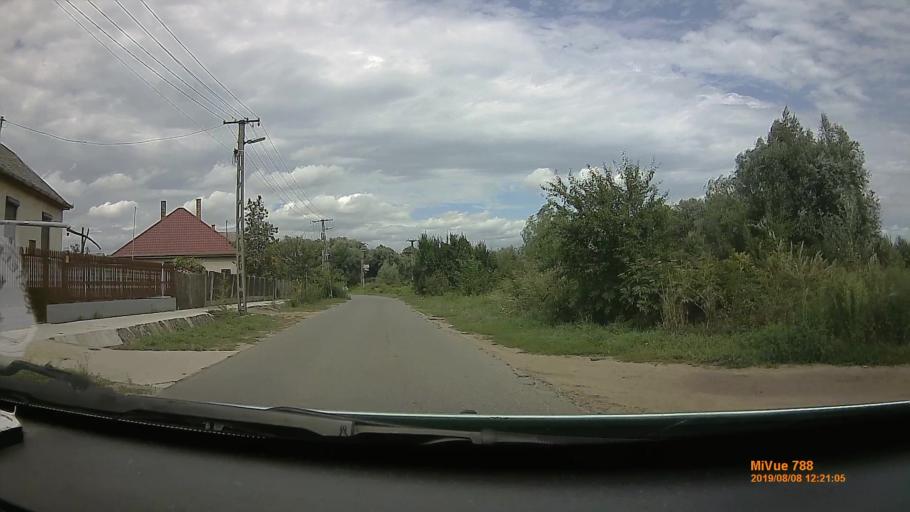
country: HU
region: Szabolcs-Szatmar-Bereg
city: Nyirbogat
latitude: 47.7918
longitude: 22.0577
